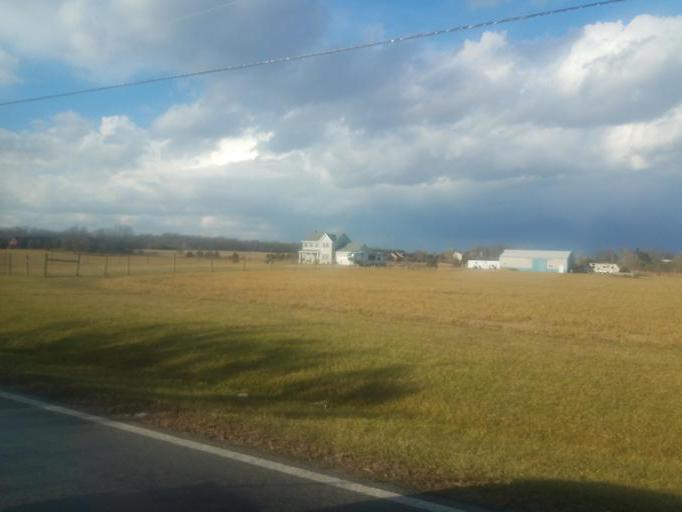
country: US
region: Ohio
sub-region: Delaware County
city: Delaware
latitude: 40.3452
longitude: -83.1385
